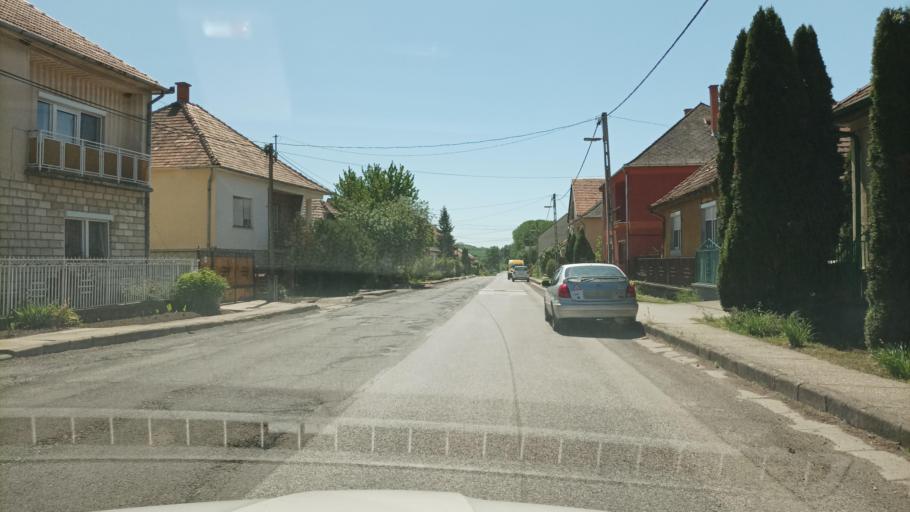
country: HU
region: Pest
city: Galgamacsa
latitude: 47.7003
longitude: 19.3975
